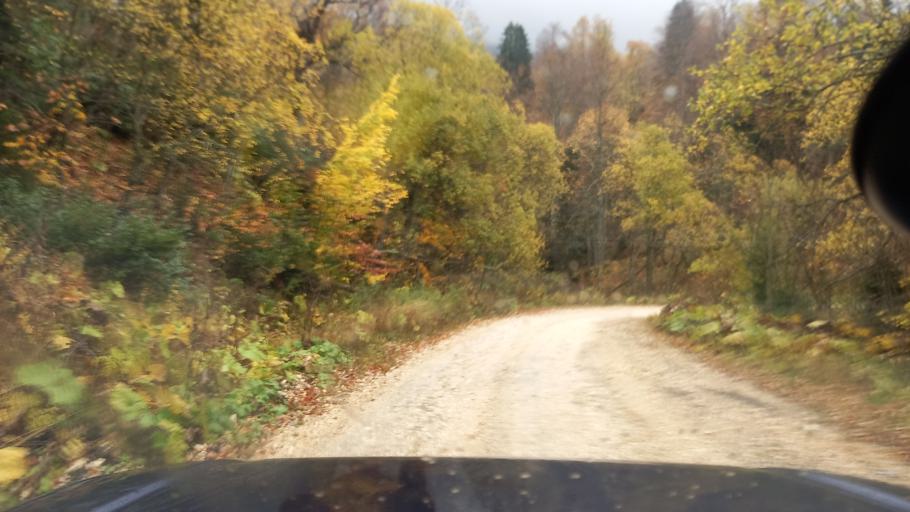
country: RU
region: Krasnodarskiy
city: Neftegorsk
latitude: 44.0189
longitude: 39.8445
